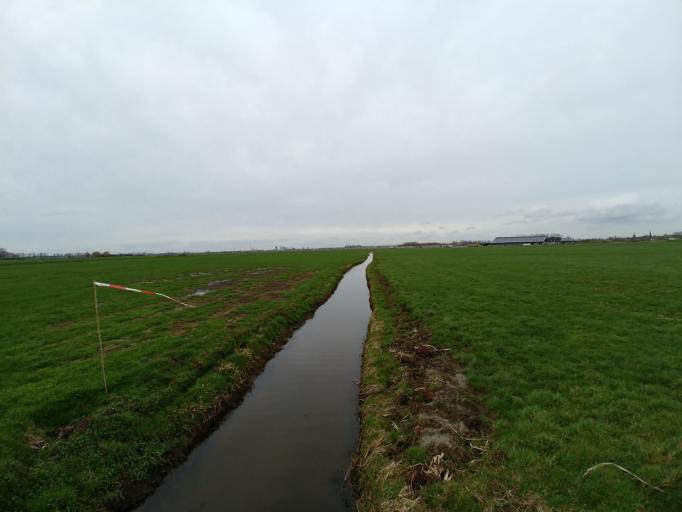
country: NL
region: North Holland
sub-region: Gemeente Amsterdam
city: Amsterdam-Zuidoost
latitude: 52.2607
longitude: 4.9543
